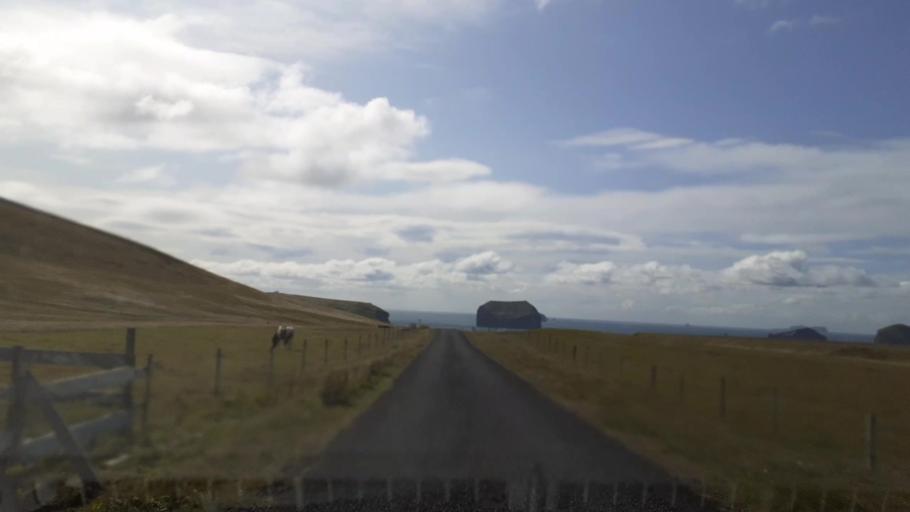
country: IS
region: South
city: Vestmannaeyjar
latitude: 63.4224
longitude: -20.2779
